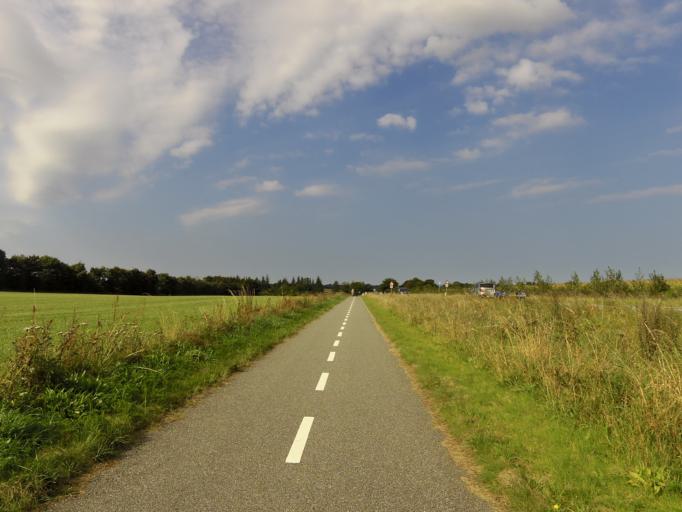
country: DK
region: South Denmark
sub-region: Vejen Kommune
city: Vejen
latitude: 55.4393
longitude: 9.1385
